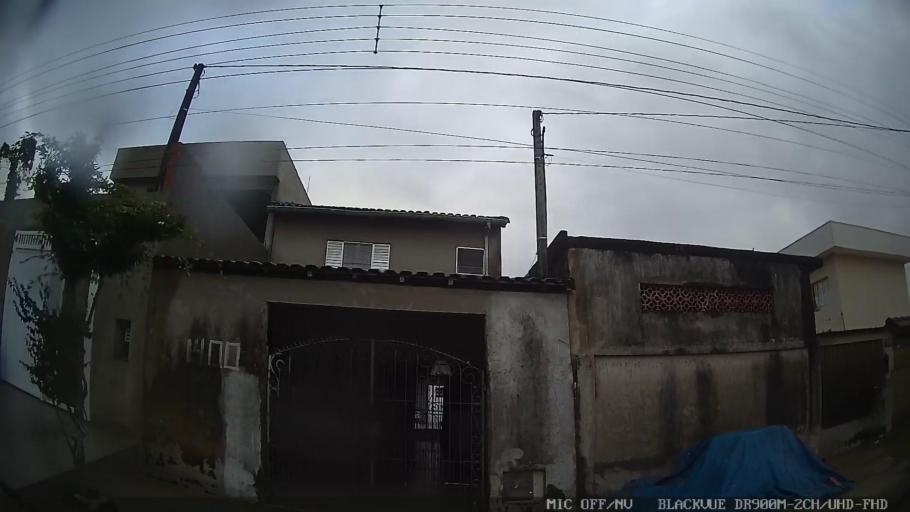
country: BR
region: Sao Paulo
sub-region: Itanhaem
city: Itanhaem
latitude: -24.1646
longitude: -46.7732
